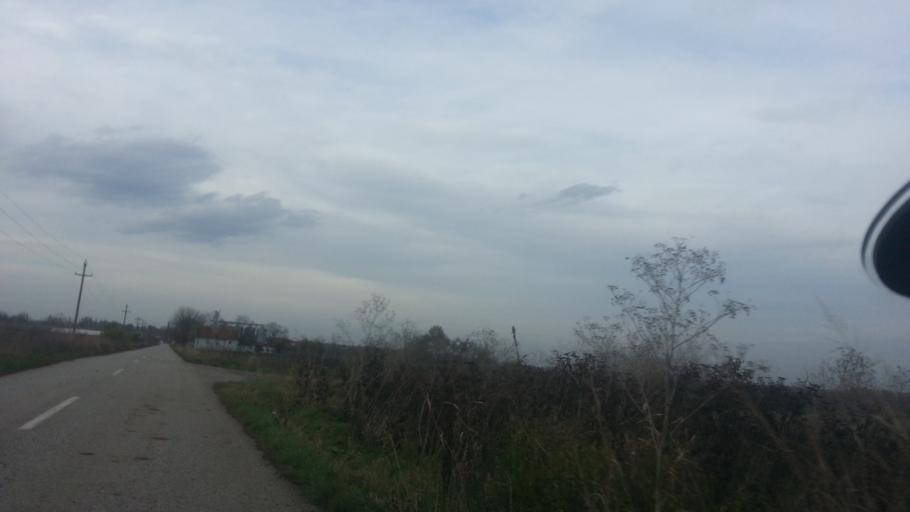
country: RS
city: Putinci
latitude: 44.9765
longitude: 19.9705
